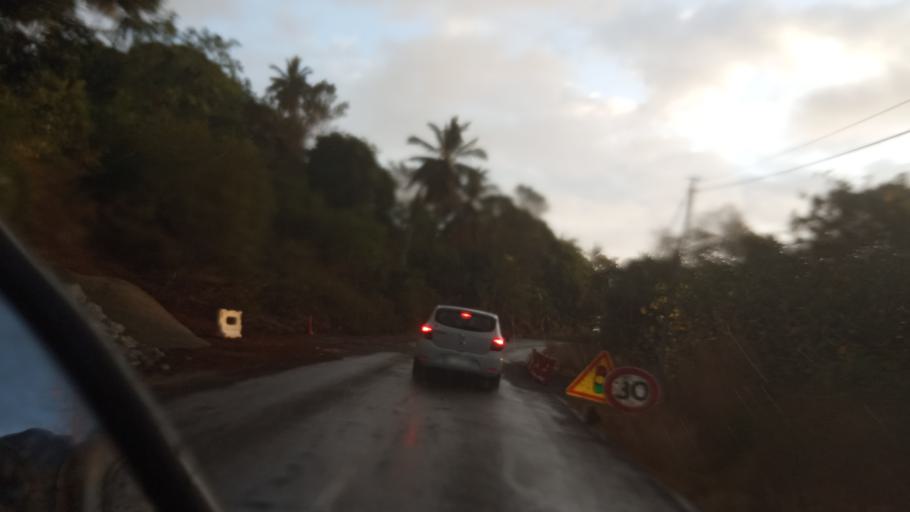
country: YT
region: Kani-Keli
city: Kani Keli
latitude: -12.9362
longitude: 45.1031
